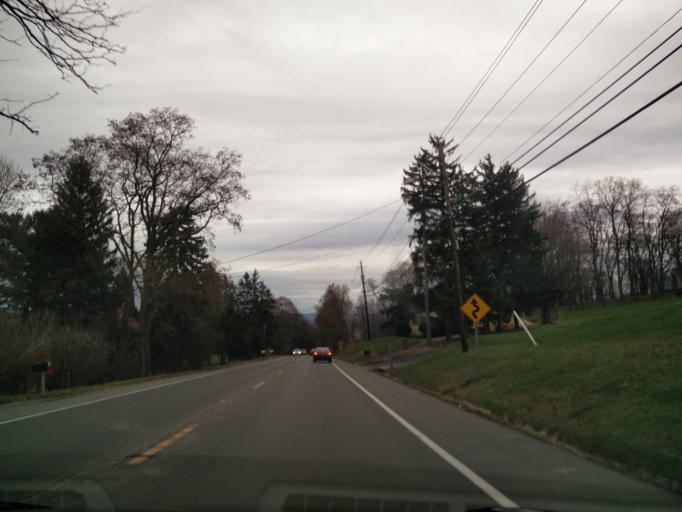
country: US
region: New York
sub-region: Tompkins County
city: Northwest Ithaca
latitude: 42.4593
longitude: -76.5277
